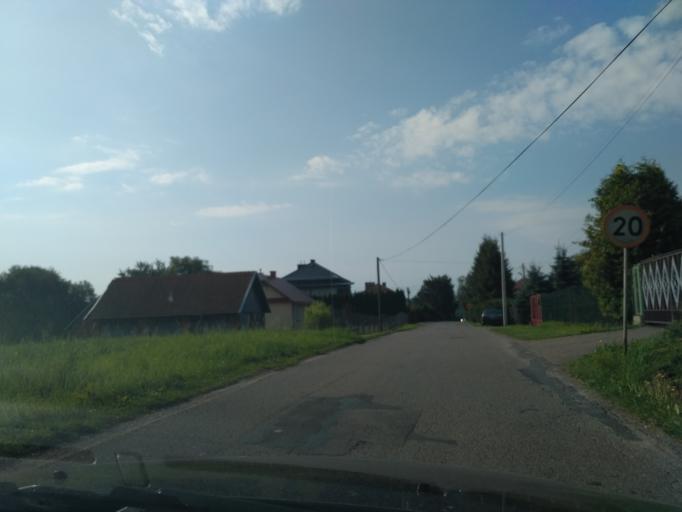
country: PL
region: Subcarpathian Voivodeship
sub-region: Powiat strzyzowski
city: Strzyzow
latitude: 49.8821
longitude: 21.7556
